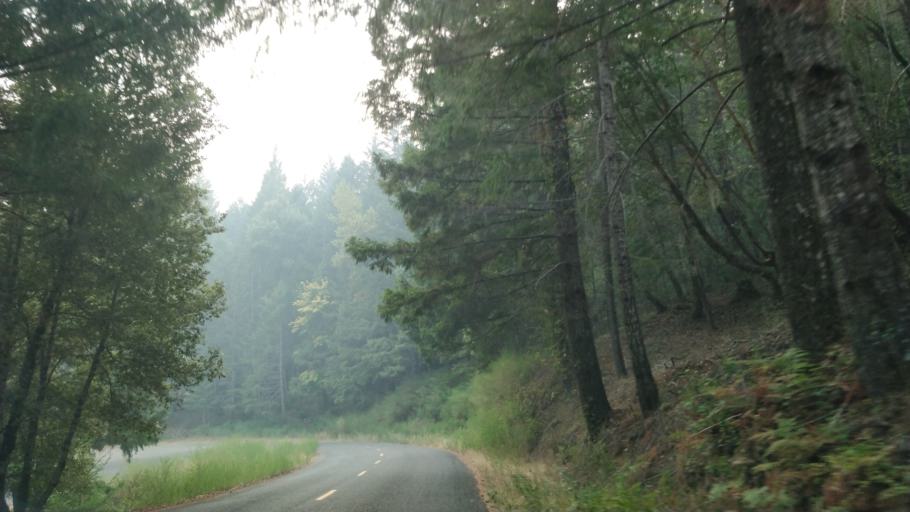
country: US
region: California
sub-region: Humboldt County
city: Rio Dell
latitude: 40.3263
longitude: -124.0427
